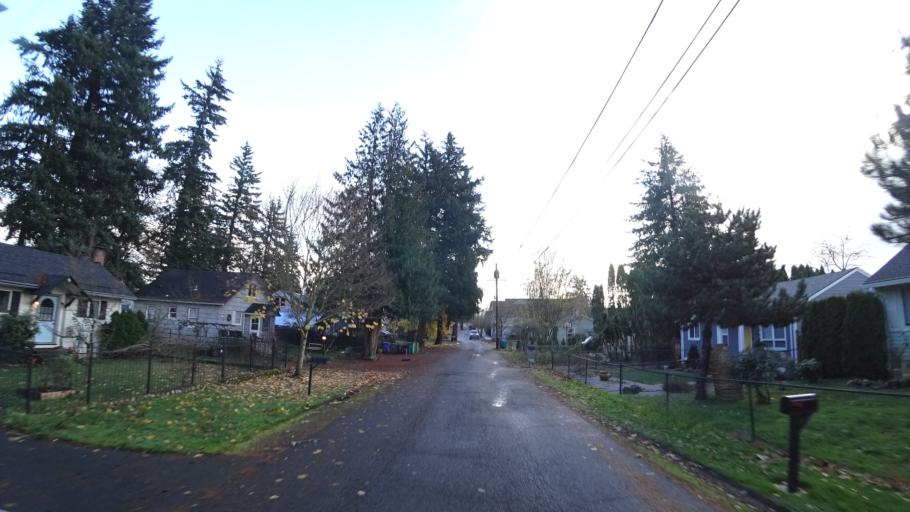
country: US
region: Oregon
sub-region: Multnomah County
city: Lents
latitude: 45.5214
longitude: -122.5339
